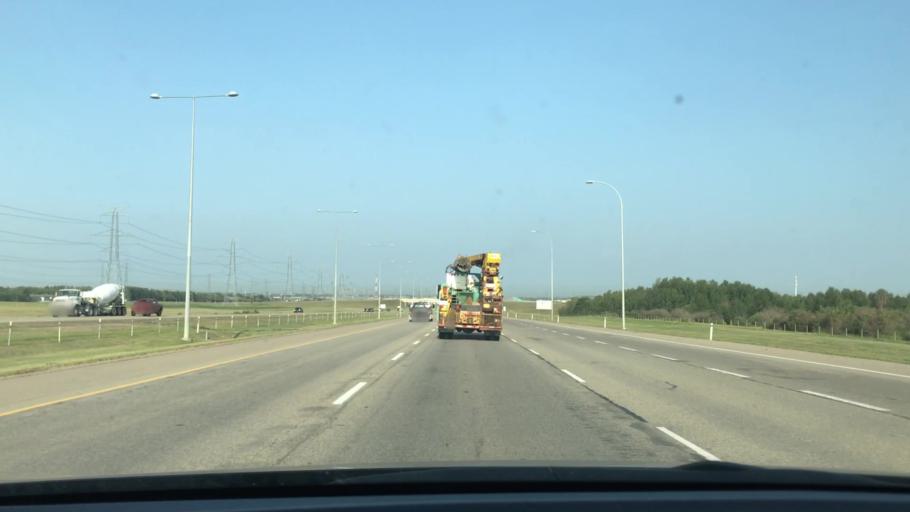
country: CA
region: Alberta
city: Beaumont
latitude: 53.4358
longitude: -113.4270
